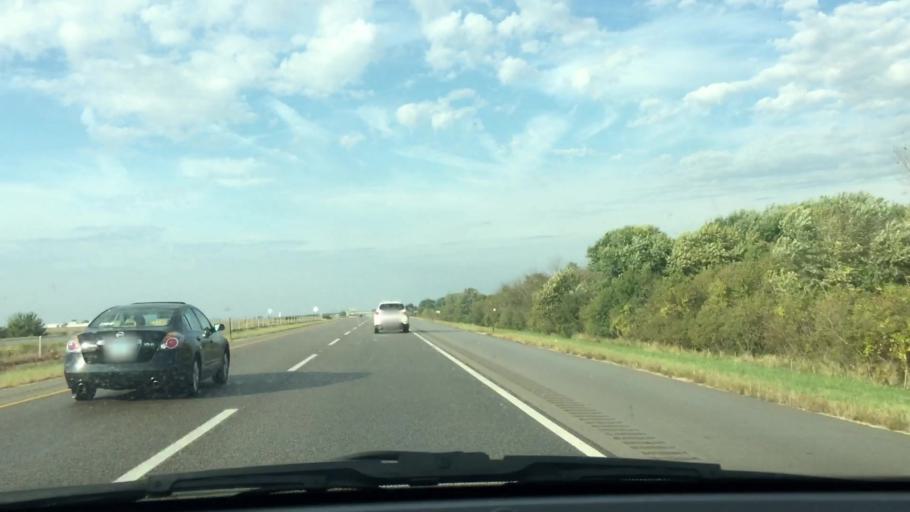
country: US
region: Illinois
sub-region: Ogle County
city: Rochelle
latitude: 41.8898
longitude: -89.0973
